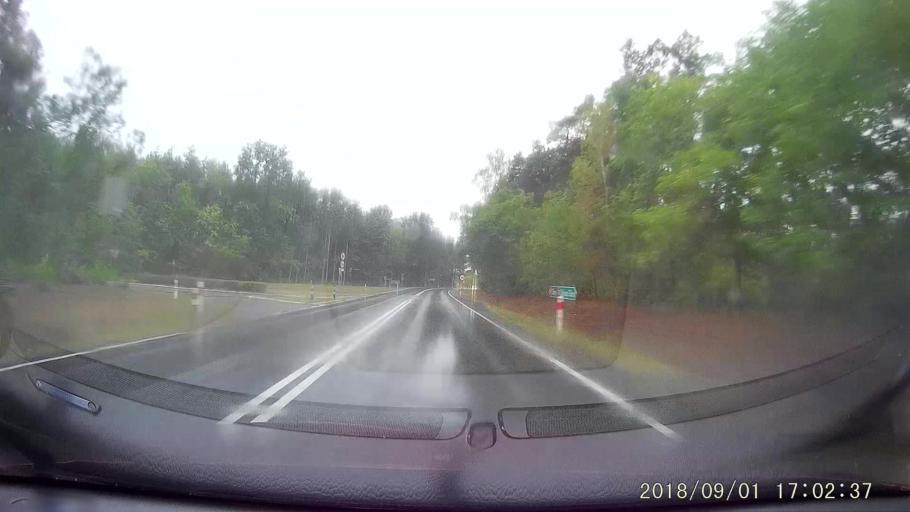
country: PL
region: Lubusz
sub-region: Powiat zielonogorski
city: Swidnica
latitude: 51.8826
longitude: 15.3796
